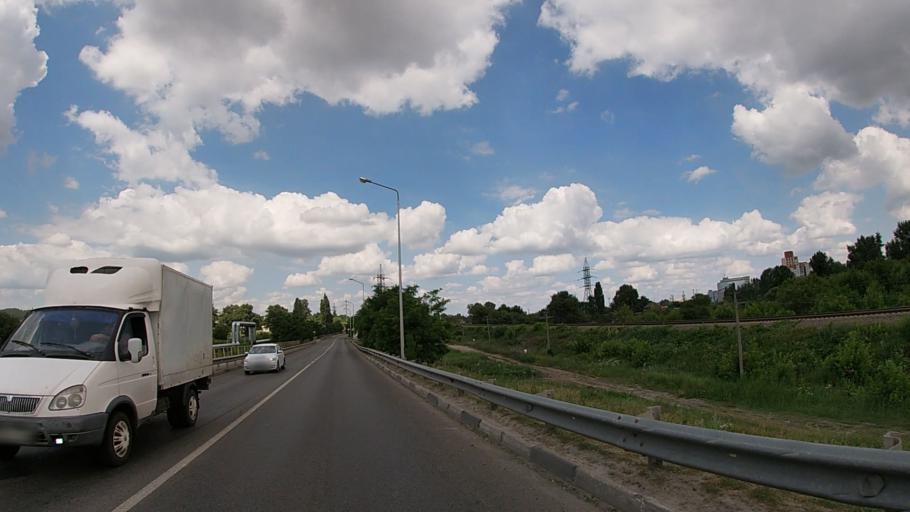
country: RU
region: Belgorod
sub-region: Belgorodskiy Rayon
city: Belgorod
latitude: 50.5913
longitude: 36.5644
